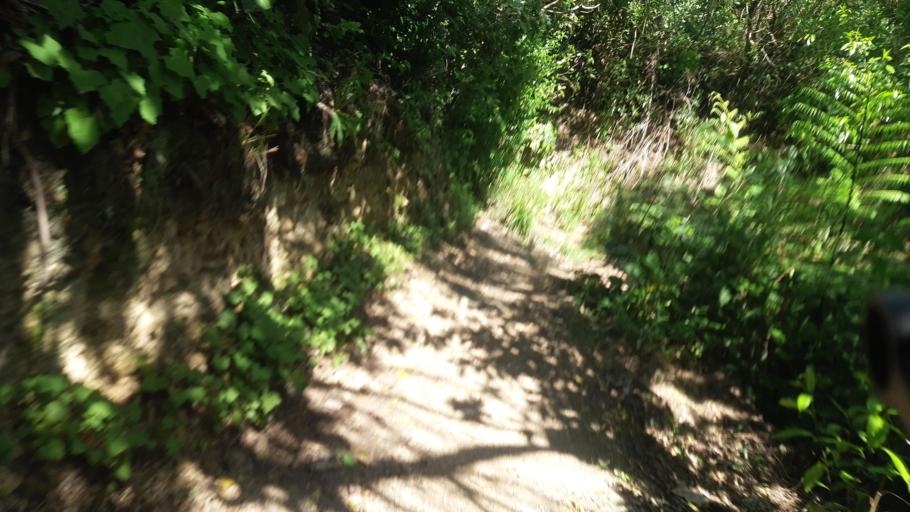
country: NZ
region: Marlborough
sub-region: Marlborough District
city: Picton
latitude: -41.2652
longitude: 174.0280
